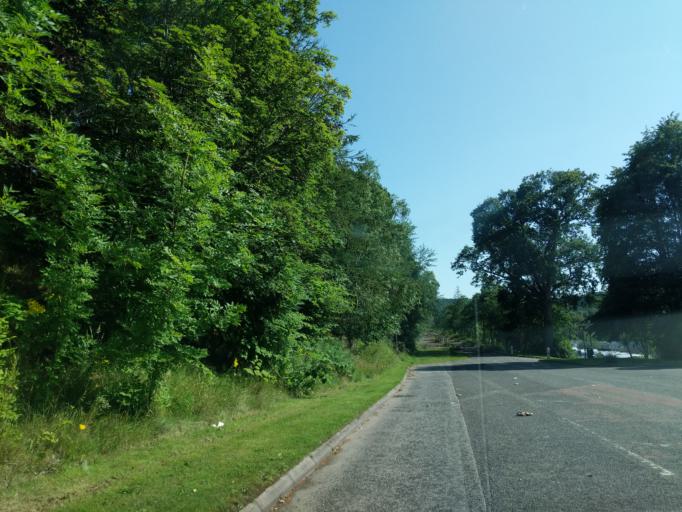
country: GB
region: Scotland
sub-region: Moray
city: Fochabers
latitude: 57.6093
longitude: -3.0886
